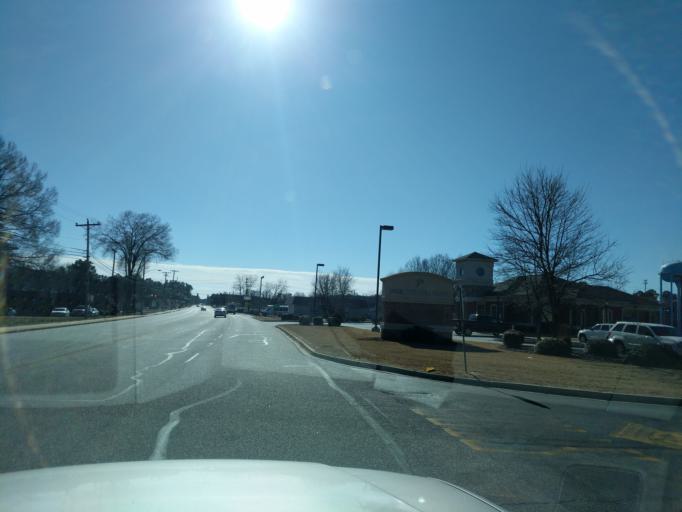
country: US
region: South Carolina
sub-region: Laurens County
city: Clinton
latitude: 34.4561
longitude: -81.8772
